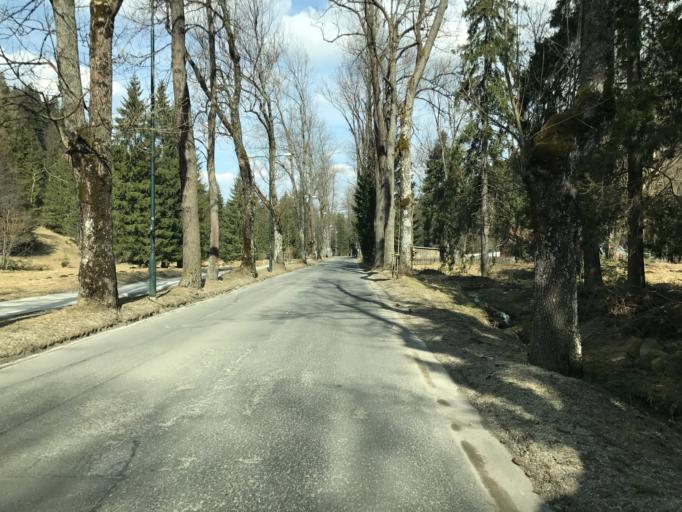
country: PL
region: Lesser Poland Voivodeship
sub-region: Powiat tatrzanski
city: Zakopane
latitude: 49.2757
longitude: 19.9810
